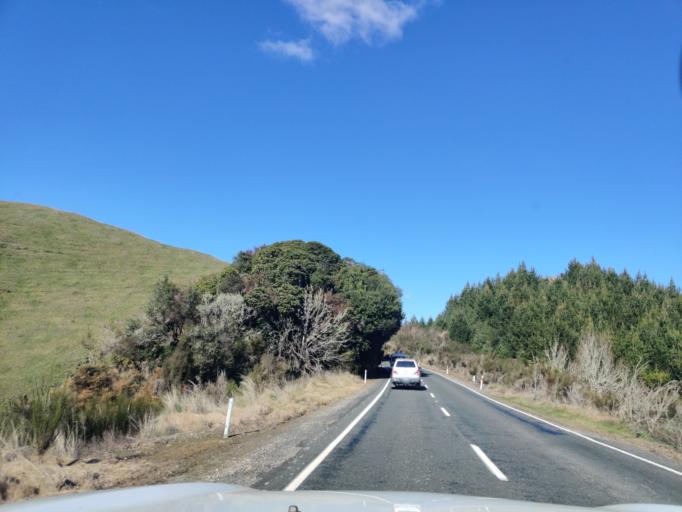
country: NZ
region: Waikato
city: Turangi
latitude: -38.7211
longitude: 175.6558
